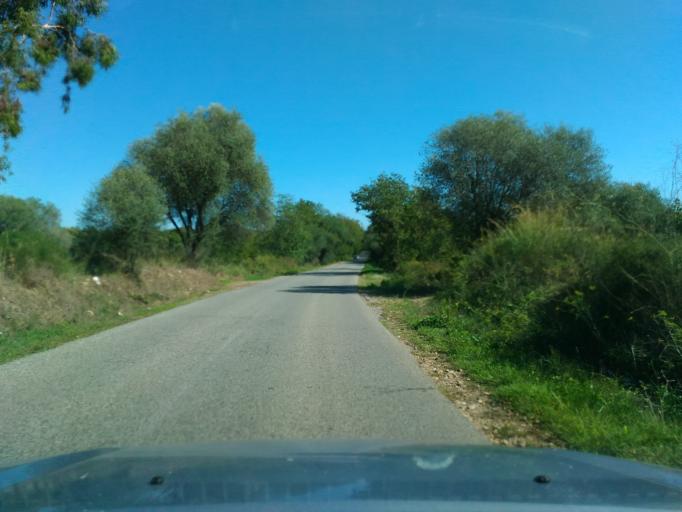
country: FR
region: Corsica
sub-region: Departement de la Haute-Corse
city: Aleria
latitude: 42.1151
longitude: 9.4830
